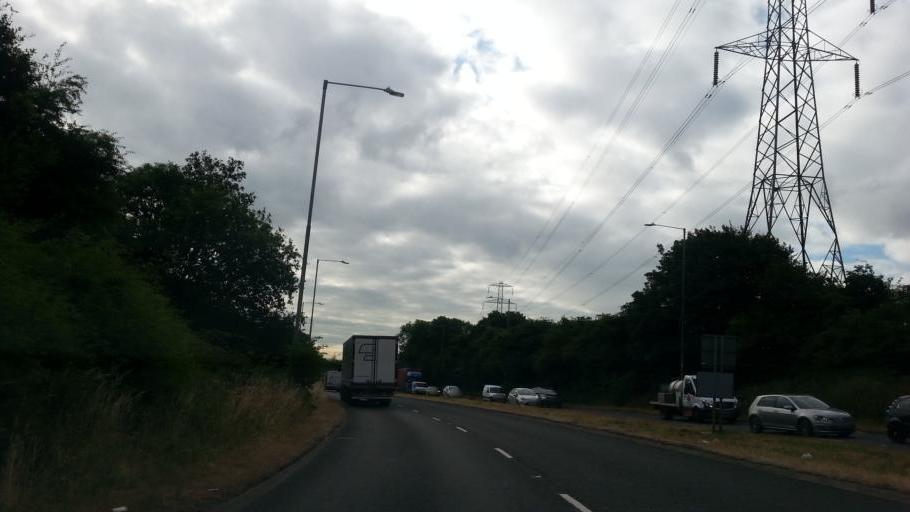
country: GB
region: England
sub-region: Warwickshire
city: Exhall
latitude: 52.4598
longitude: -1.4915
